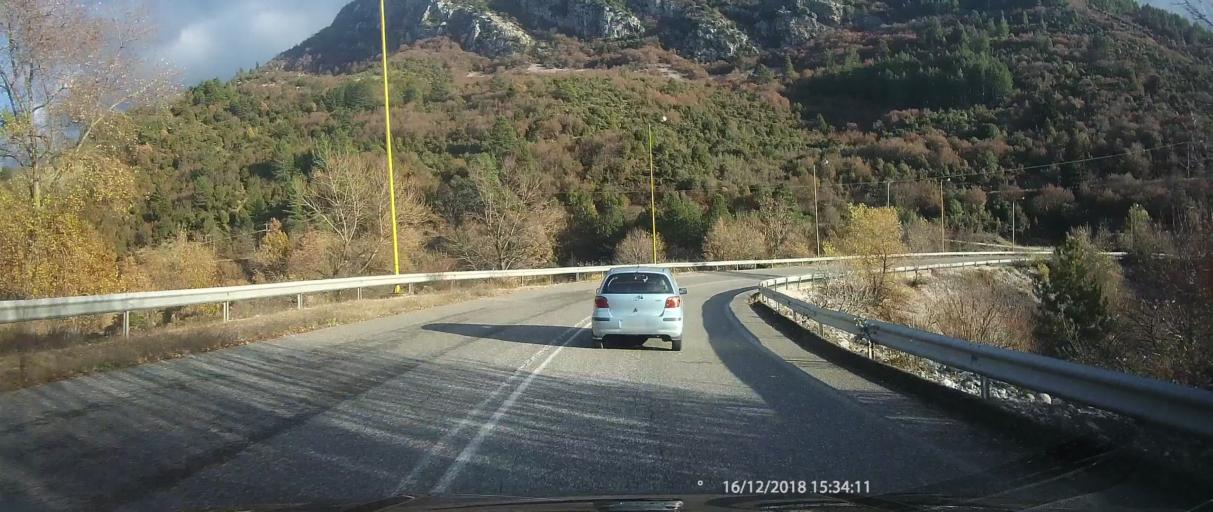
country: GR
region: Epirus
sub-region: Nomos Ioanninon
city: Konitsa
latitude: 40.0636
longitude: 20.7415
